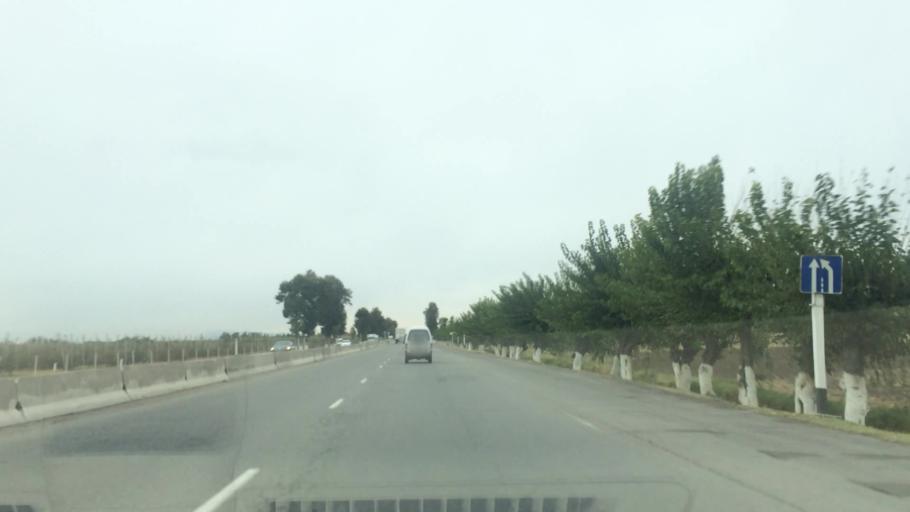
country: UZ
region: Samarqand
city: Bulung'ur
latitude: 39.7383
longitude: 67.1804
